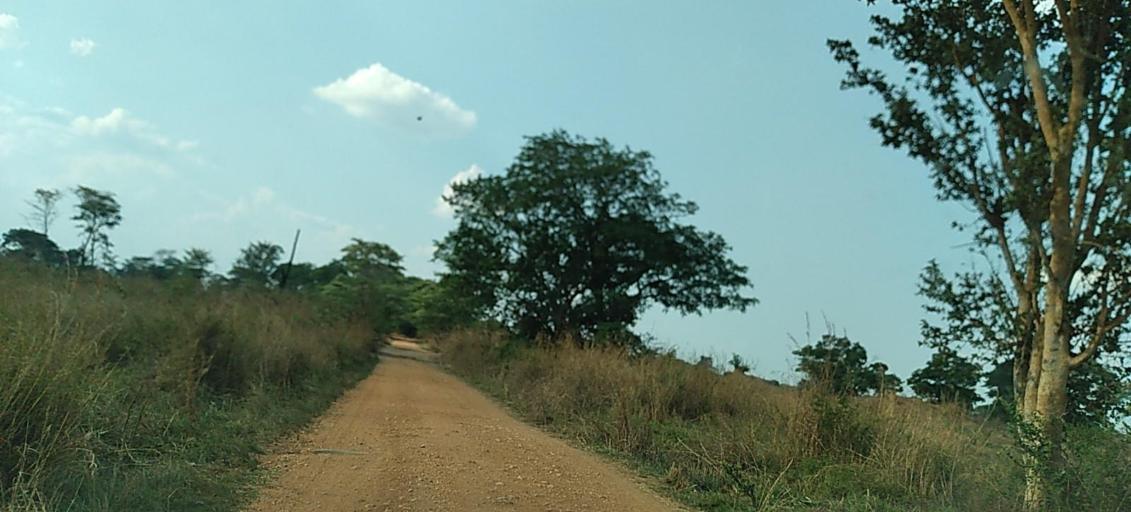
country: ZM
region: Copperbelt
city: Mpongwe
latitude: -13.4972
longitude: 28.0874
